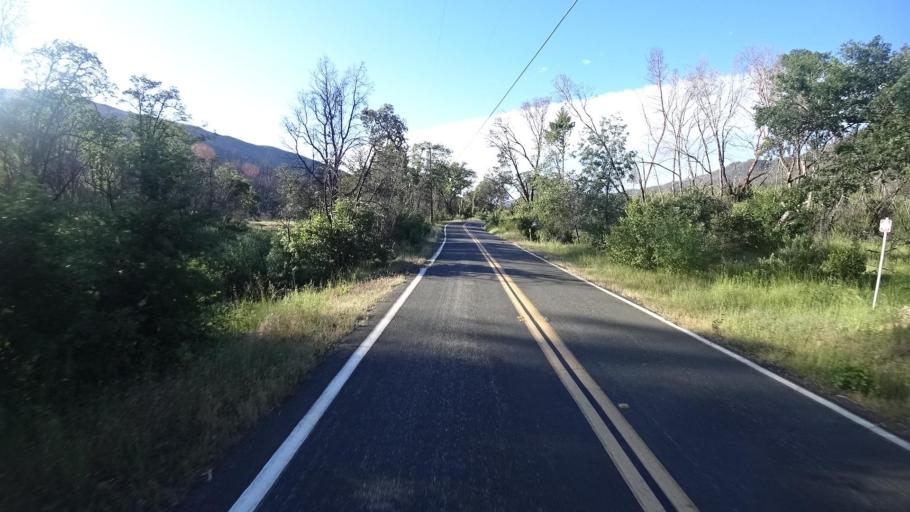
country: US
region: California
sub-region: Lake County
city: Upper Lake
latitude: 39.2376
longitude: -122.9458
